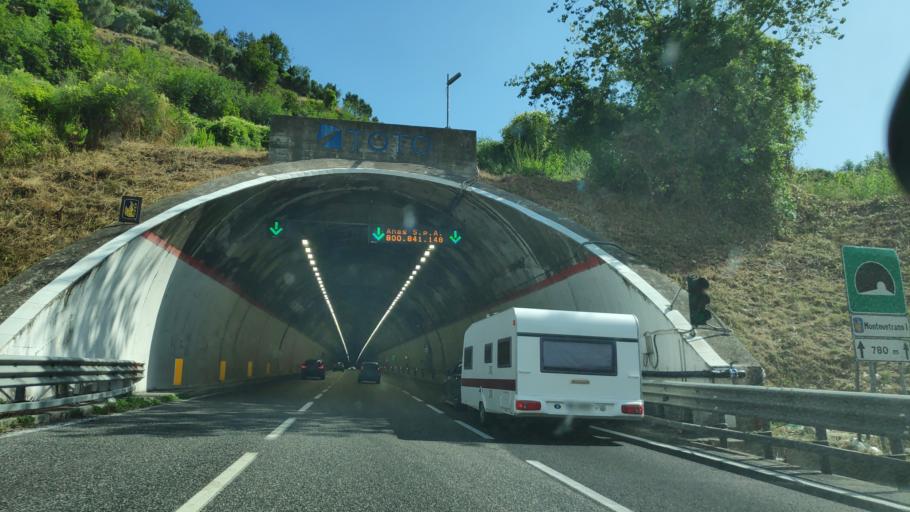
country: IT
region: Campania
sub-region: Provincia di Salerno
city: Pezzano-Filetta
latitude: 40.6775
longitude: 14.8573
